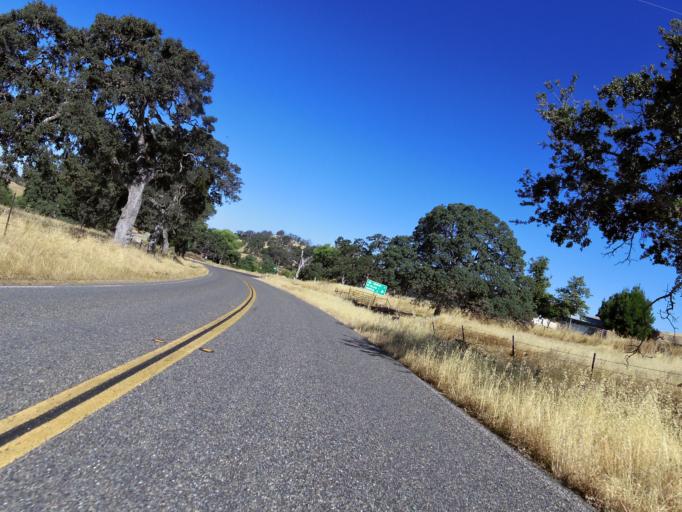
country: US
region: California
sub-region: Mariposa County
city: Mariposa
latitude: 37.4917
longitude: -120.1403
